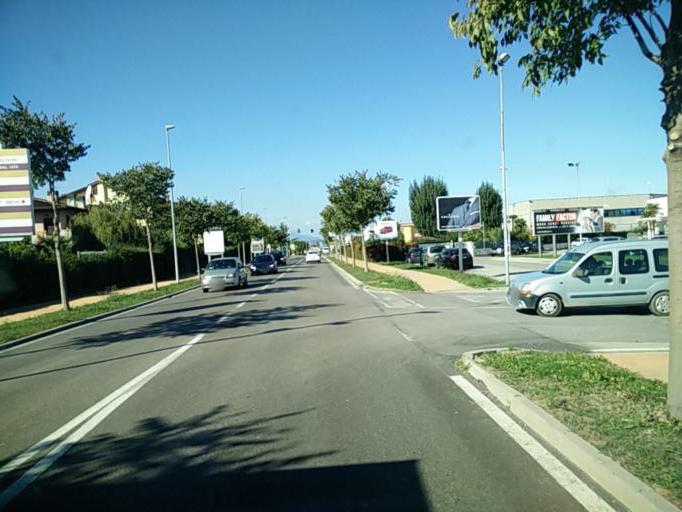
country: IT
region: Lombardy
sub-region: Provincia di Brescia
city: San Martino della Battaglia
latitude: 45.4401
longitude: 10.6018
